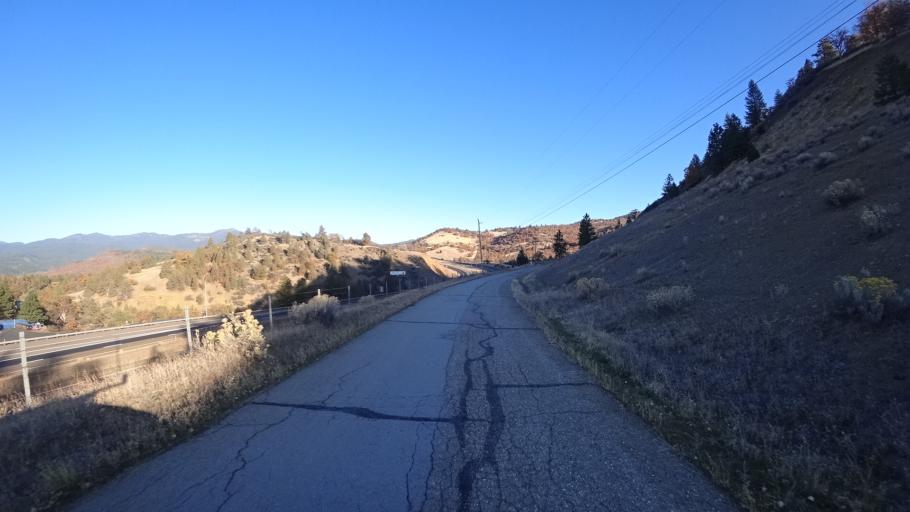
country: US
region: Oregon
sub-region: Jackson County
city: Ashland
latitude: 41.9950
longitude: -122.6093
